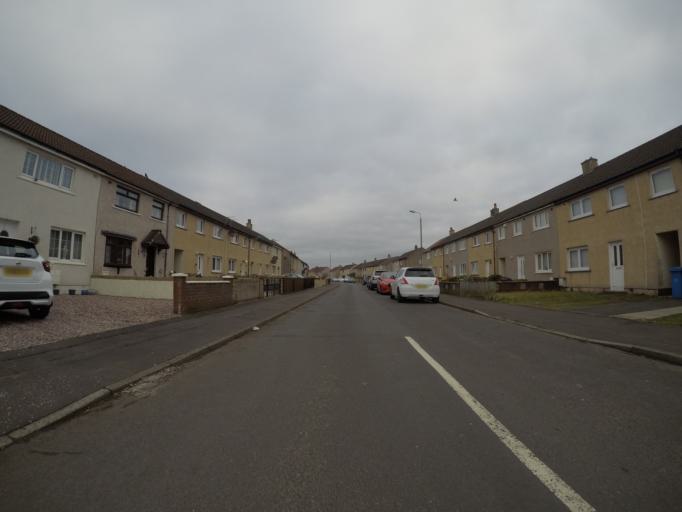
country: GB
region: Scotland
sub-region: North Ayrshire
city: Irvine
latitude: 55.6255
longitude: -4.6663
